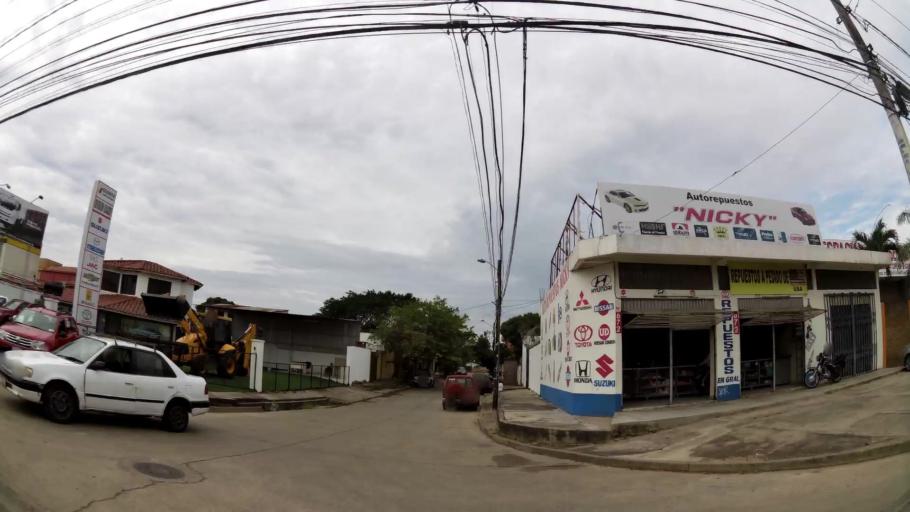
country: BO
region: Santa Cruz
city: Santa Cruz de la Sierra
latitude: -17.7536
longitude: -63.1598
